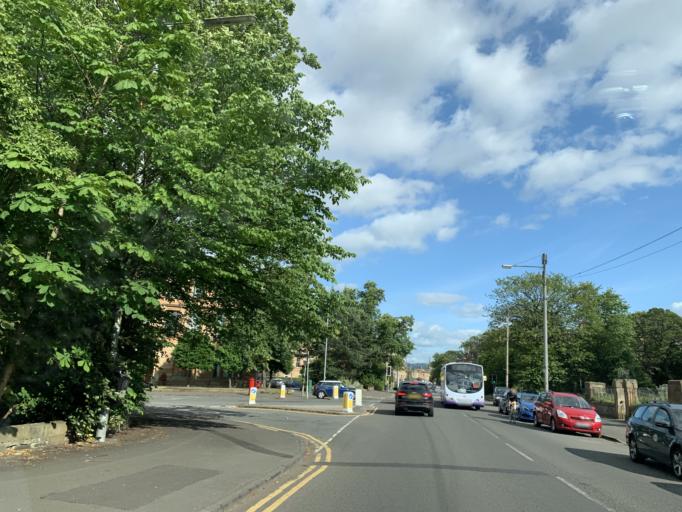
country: GB
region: Scotland
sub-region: Glasgow City
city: Glasgow
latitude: 55.8404
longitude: -4.2780
